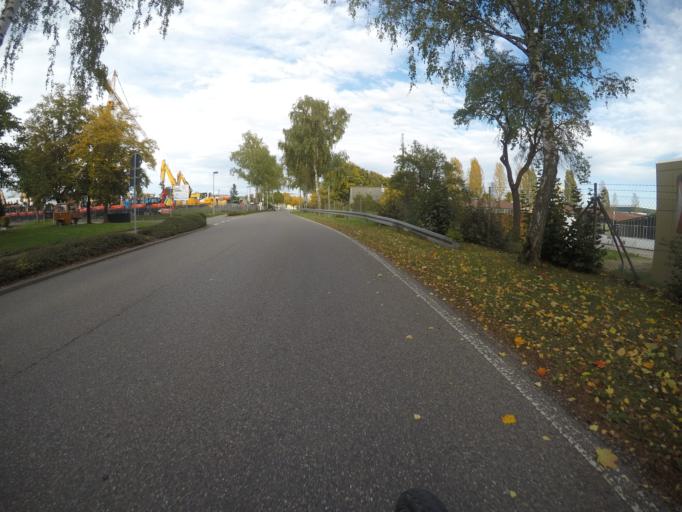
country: DE
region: Baden-Wuerttemberg
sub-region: Regierungsbezirk Stuttgart
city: Herrenberg
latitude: 48.5759
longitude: 8.8879
